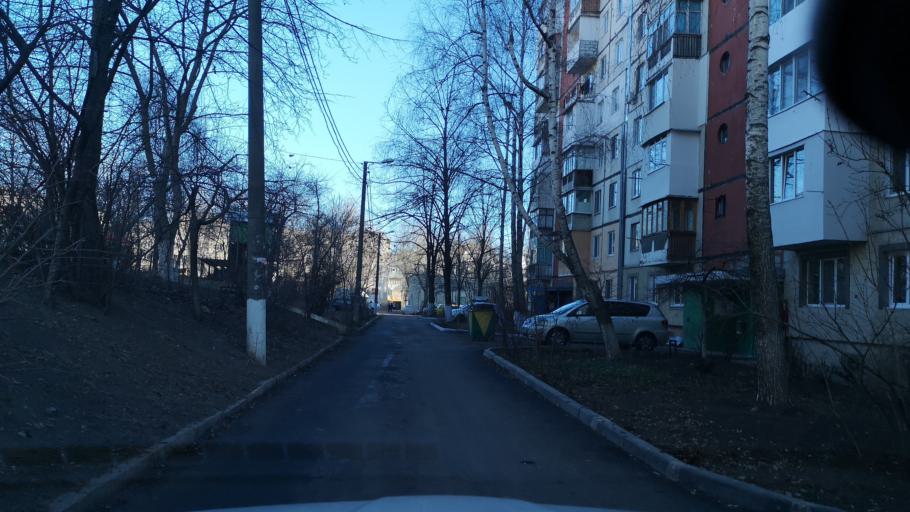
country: MD
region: Chisinau
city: Chisinau
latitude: 47.0333
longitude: 28.8798
